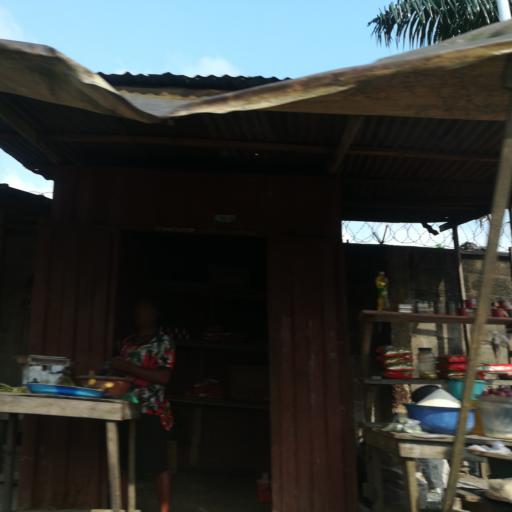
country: NG
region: Rivers
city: Okrika
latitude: 4.7798
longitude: 7.1362
